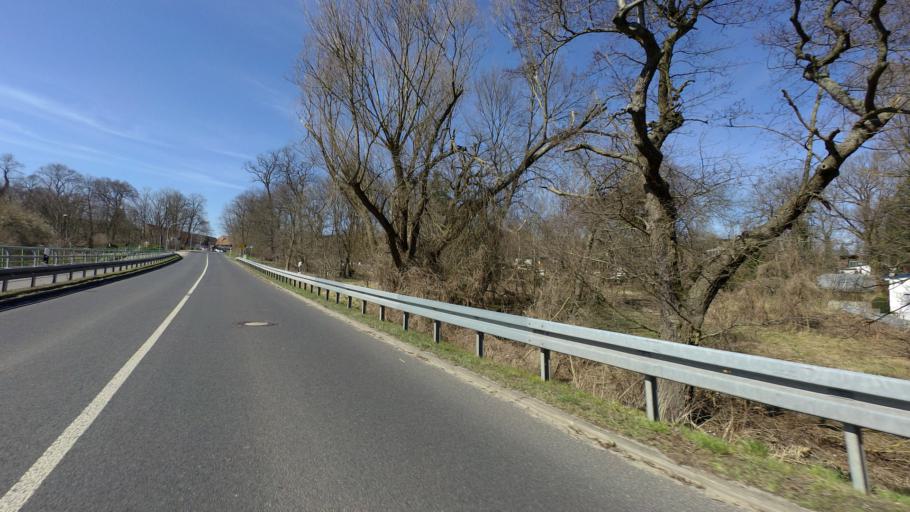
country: DE
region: Brandenburg
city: Furstenwalde
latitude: 52.4021
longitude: 14.0447
